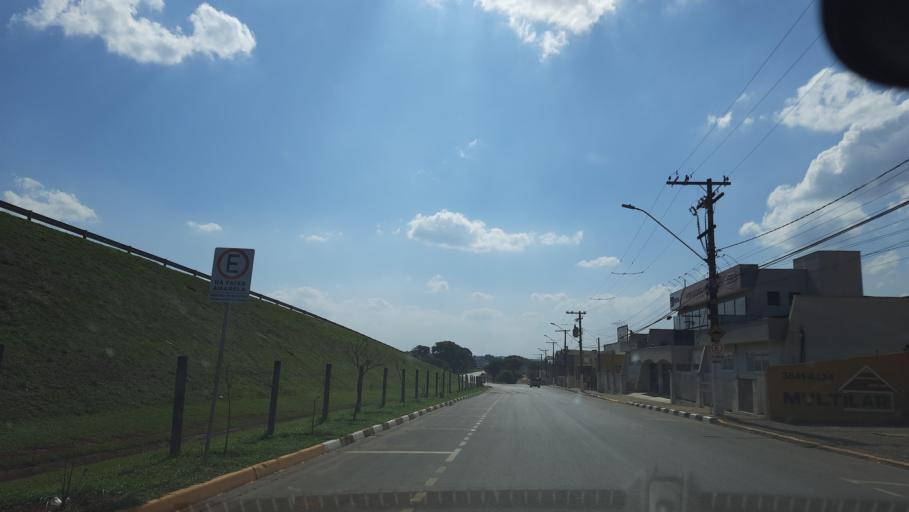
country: BR
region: Sao Paulo
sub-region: Vargem Grande Do Sul
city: Vargem Grande do Sul
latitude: -21.8401
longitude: -46.9089
